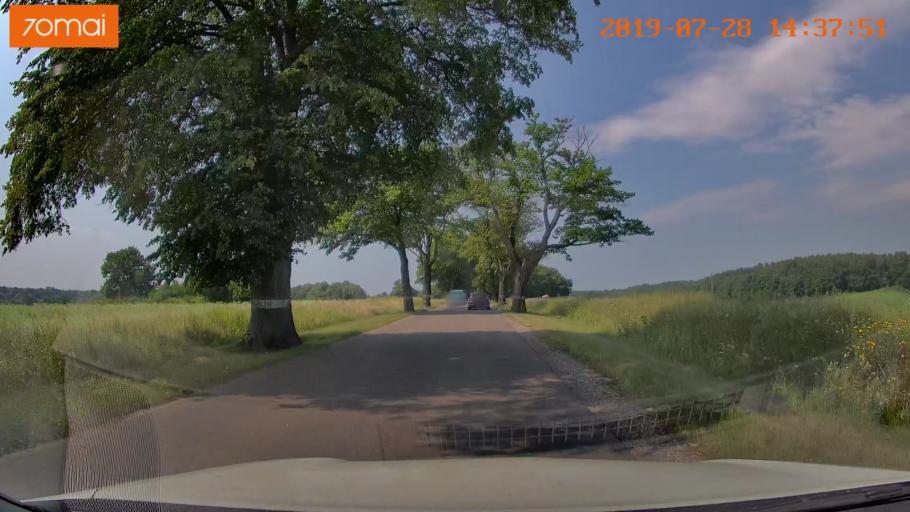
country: RU
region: Kaliningrad
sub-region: Gorod Kaliningrad
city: Yantarnyy
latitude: 54.8420
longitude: 19.9917
